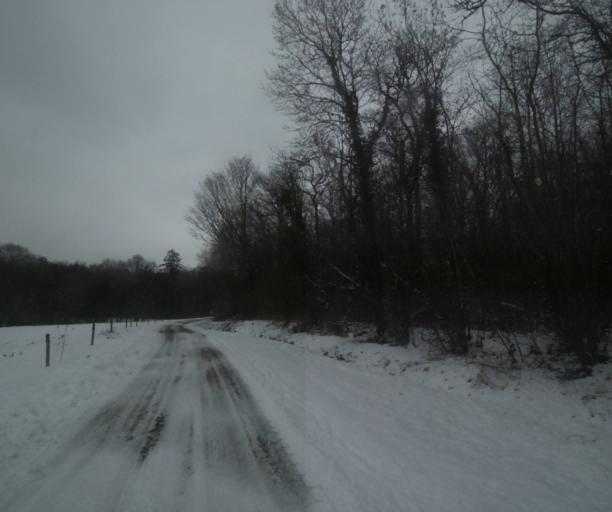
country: FR
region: Champagne-Ardenne
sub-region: Departement de la Haute-Marne
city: Laneuville-a-Remy
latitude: 48.4668
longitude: 4.8979
